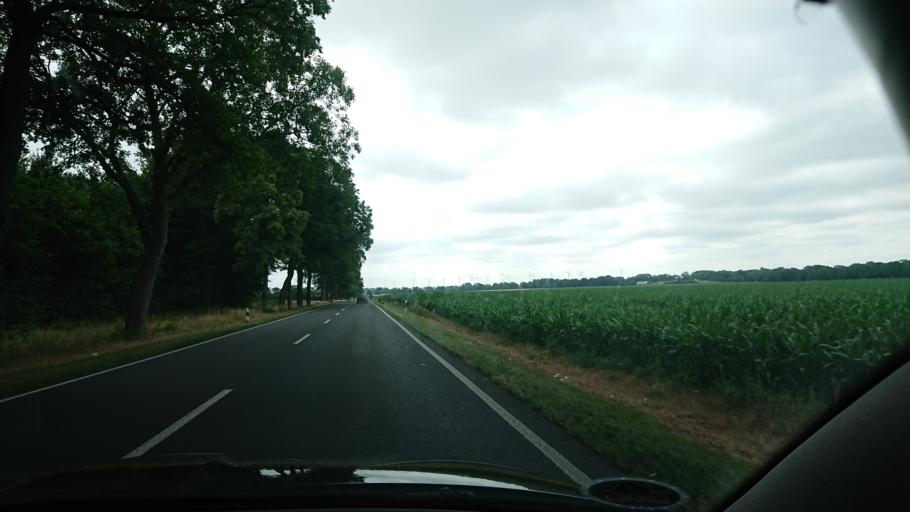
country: DE
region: Brandenburg
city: Plattenburg
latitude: 53.0070
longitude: 12.0390
